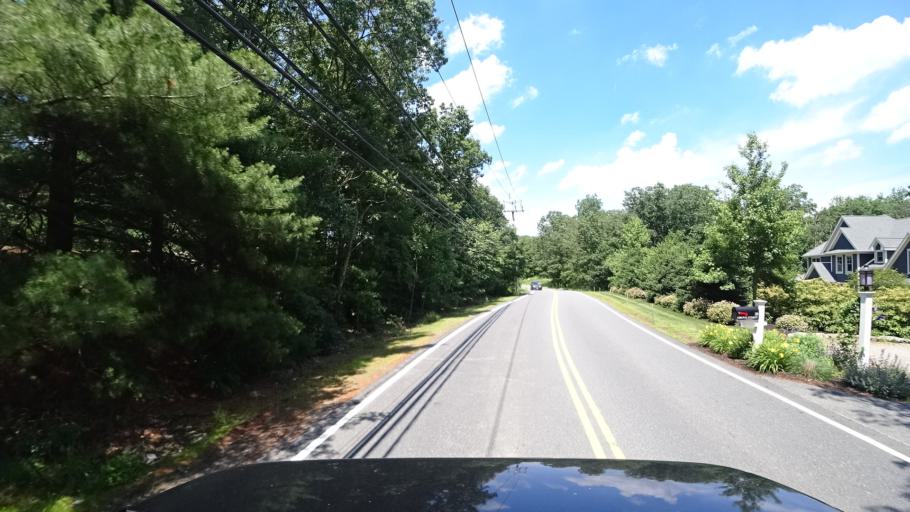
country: US
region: Massachusetts
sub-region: Norfolk County
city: Westwood
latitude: 42.2432
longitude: -71.2095
